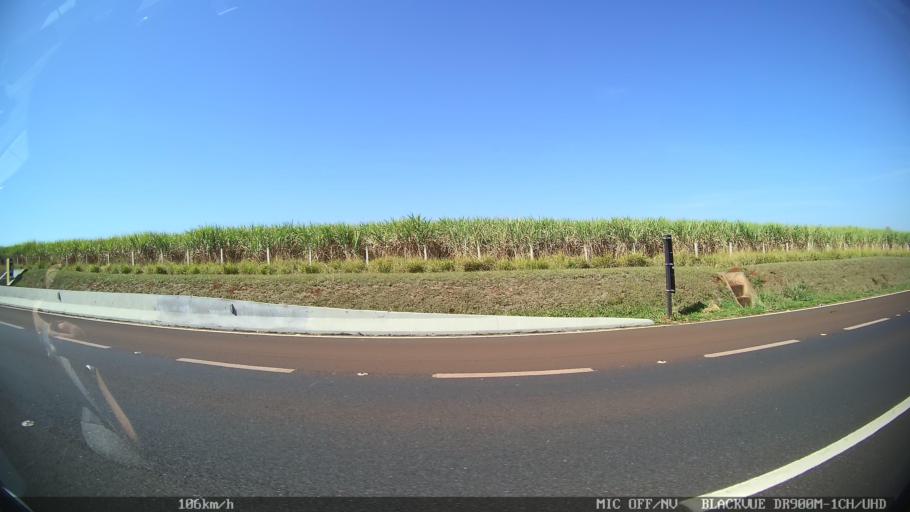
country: BR
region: Sao Paulo
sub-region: Batatais
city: Batatais
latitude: -20.7834
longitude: -47.5528
